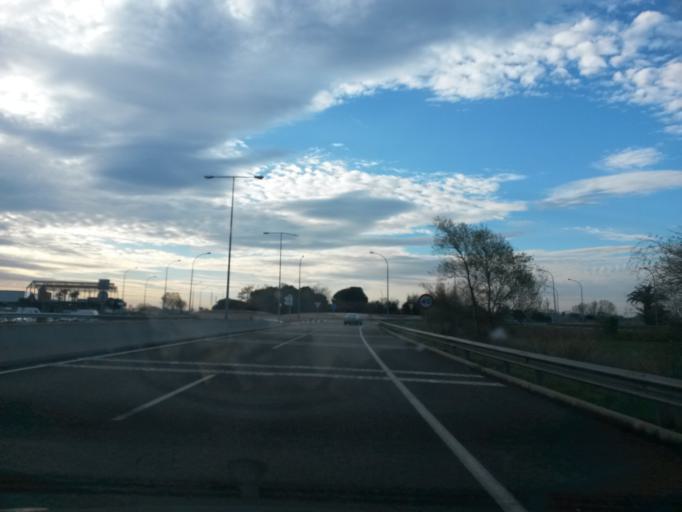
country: ES
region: Catalonia
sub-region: Provincia de Girona
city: Vila-sacra
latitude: 42.2630
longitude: 3.0357
